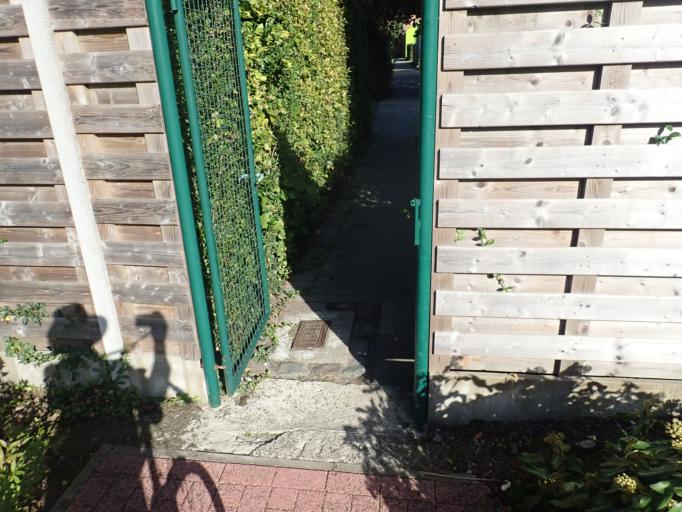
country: BE
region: Flanders
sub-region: Provincie Antwerpen
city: Zoersel
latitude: 51.2694
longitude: 4.7111
